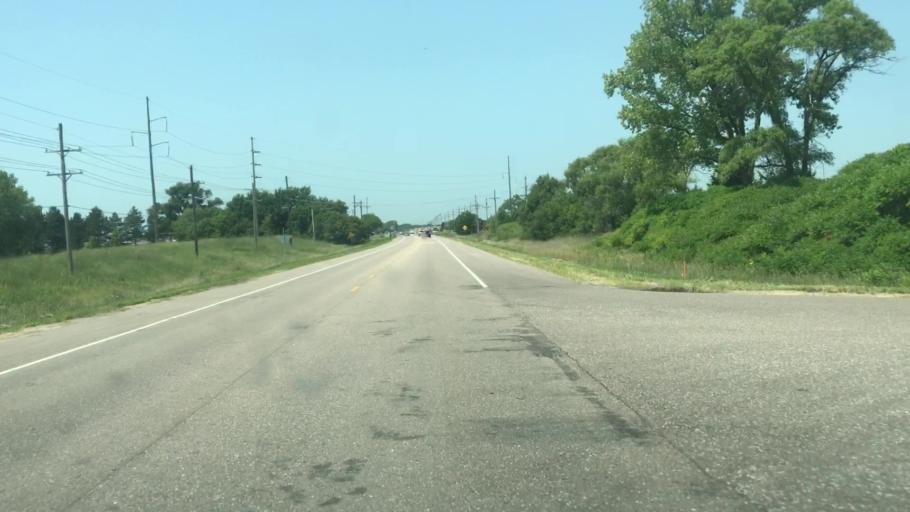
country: US
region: Nebraska
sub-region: Hall County
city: Grand Island
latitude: 40.8878
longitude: -98.3650
